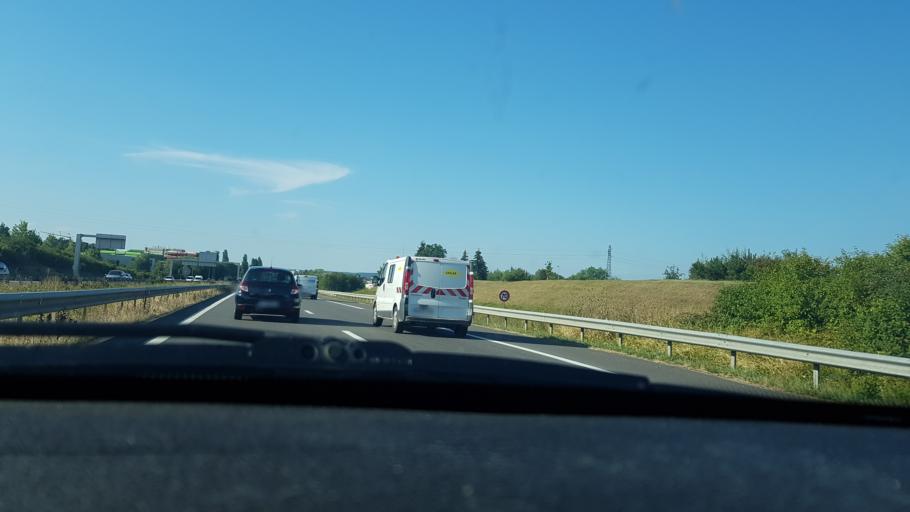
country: FR
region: Lorraine
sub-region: Departement de Meurthe-et-Moselle
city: Vandoeuvre-les-Nancy
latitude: 48.6365
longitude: 6.1818
